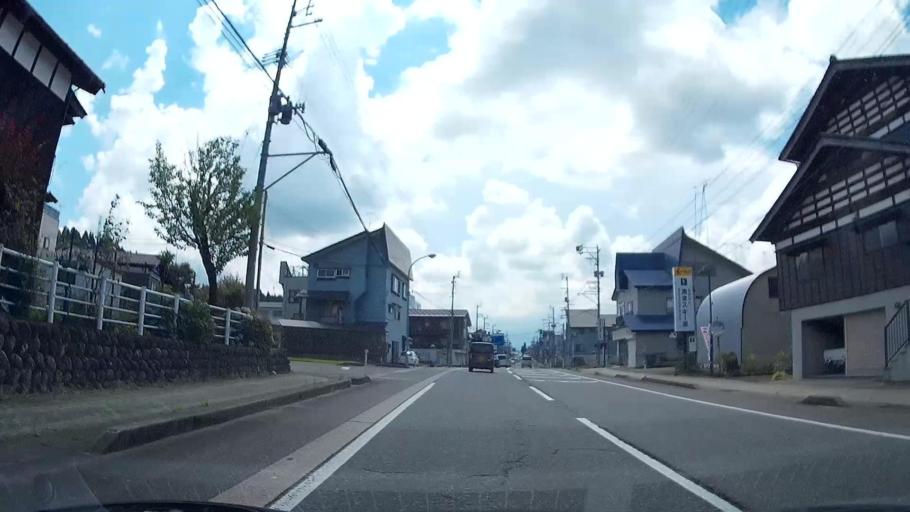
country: JP
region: Niigata
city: Tokamachi
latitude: 37.0543
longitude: 138.6996
